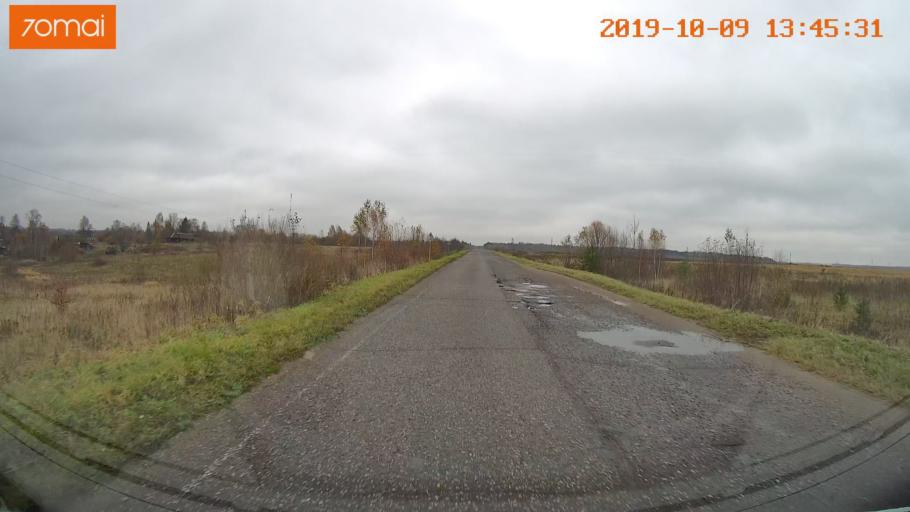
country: RU
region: Kostroma
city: Buy
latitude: 58.3749
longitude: 41.2106
